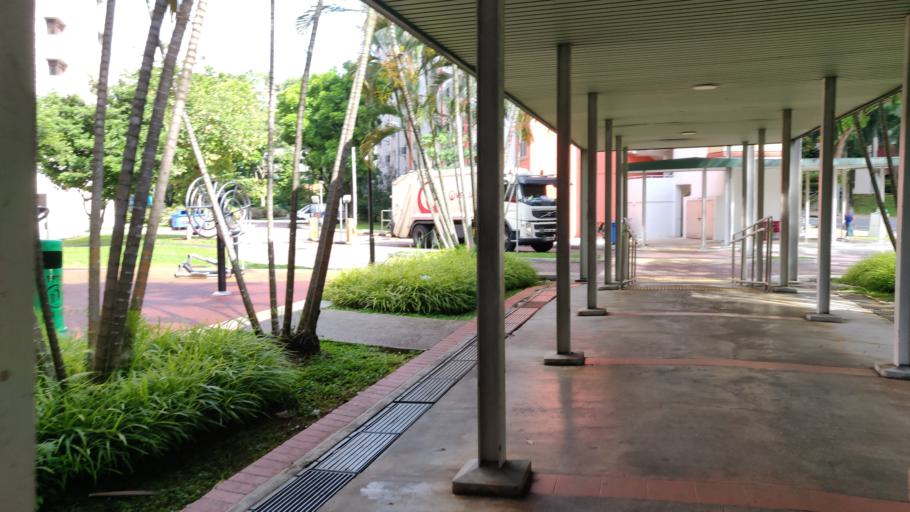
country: SG
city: Singapore
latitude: 1.2876
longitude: 103.8169
